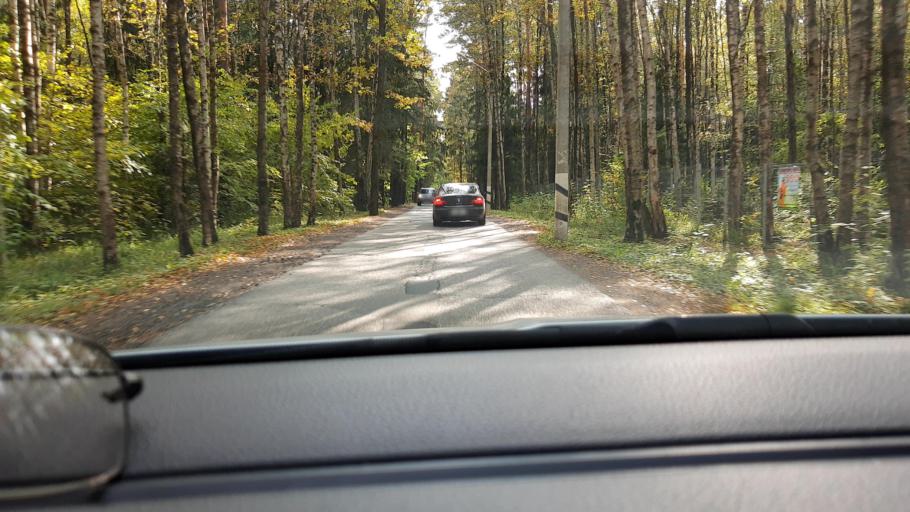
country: RU
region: Moskovskaya
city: Barvikha
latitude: 55.7186
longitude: 37.3041
